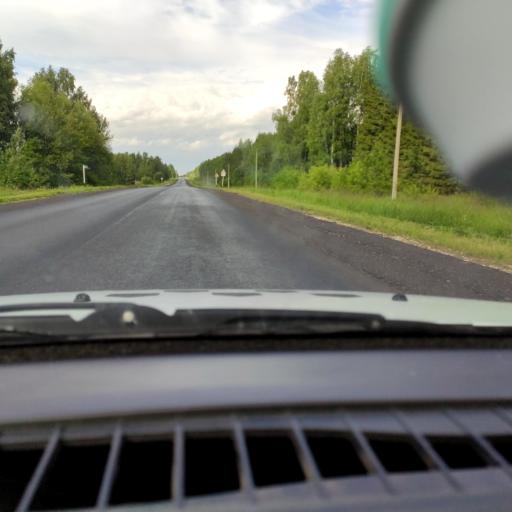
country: RU
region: Perm
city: Orda
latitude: 57.2242
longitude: 56.9567
